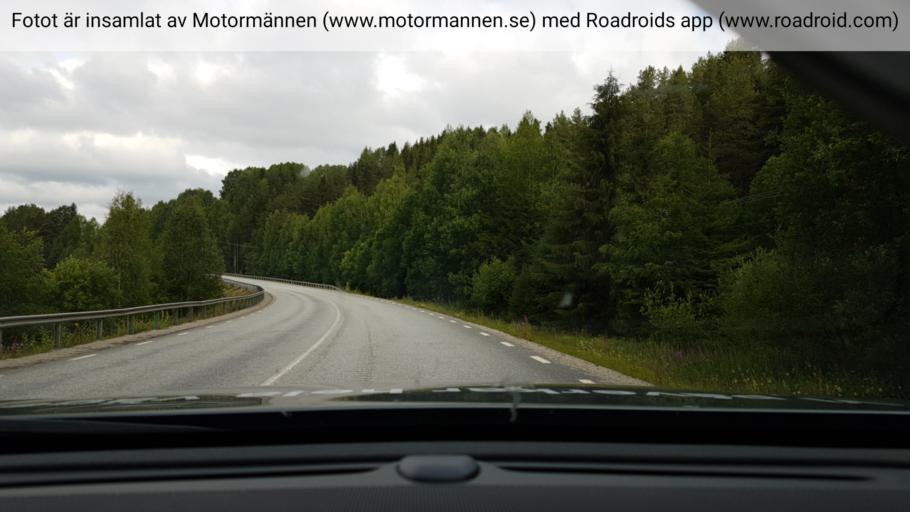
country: SE
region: Vaesterbotten
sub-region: Vindelns Kommun
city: Vindeln
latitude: 64.3116
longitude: 19.6065
